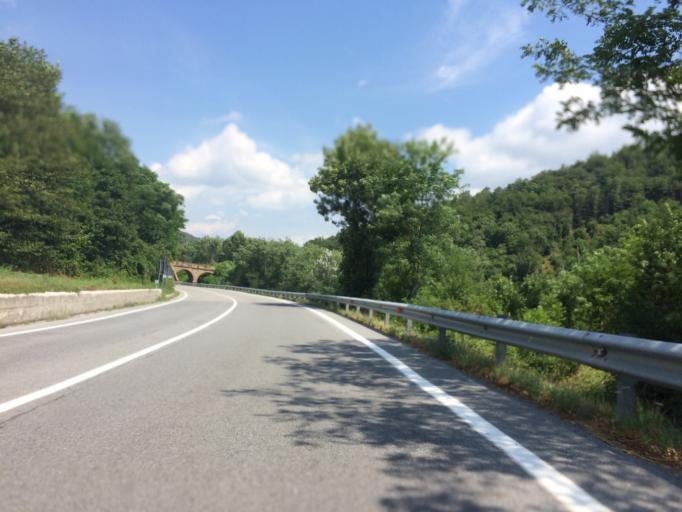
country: IT
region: Piedmont
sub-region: Provincia di Cuneo
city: Priola
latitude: 44.2293
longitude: 8.0174
